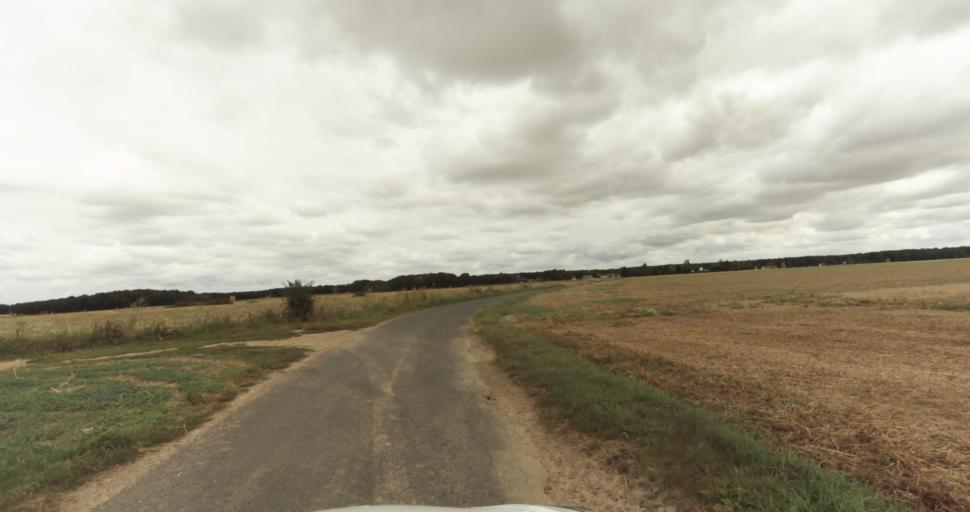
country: FR
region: Haute-Normandie
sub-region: Departement de l'Eure
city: Tillieres-sur-Avre
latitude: 48.7892
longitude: 1.0996
